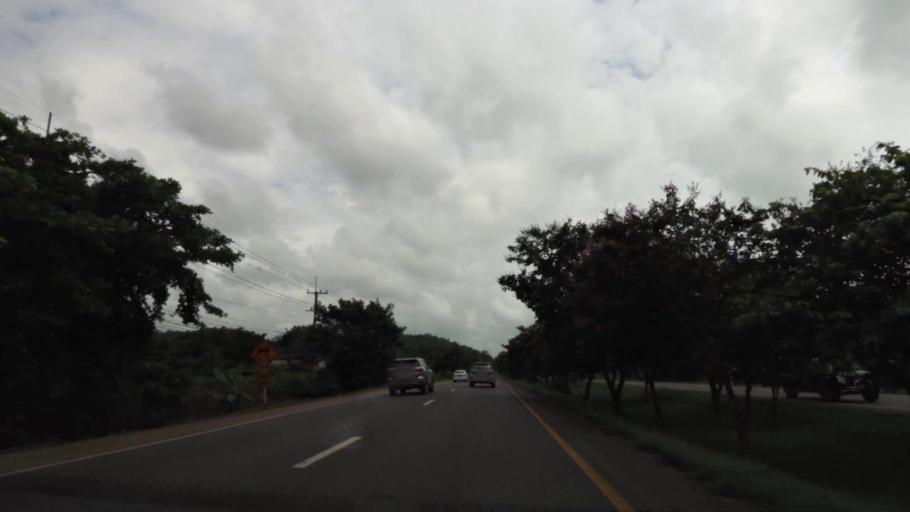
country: TH
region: Chanthaburi
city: Na Yai Am
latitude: 12.7370
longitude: 101.8962
